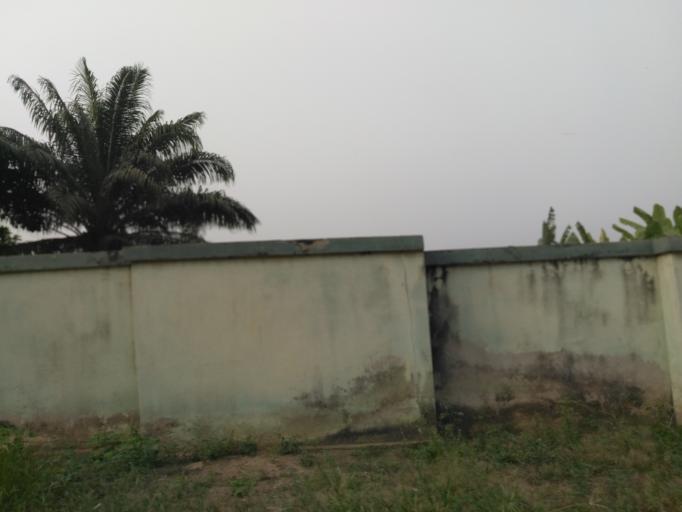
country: GH
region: Ashanti
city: Kumasi
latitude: 6.6527
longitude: -1.6203
